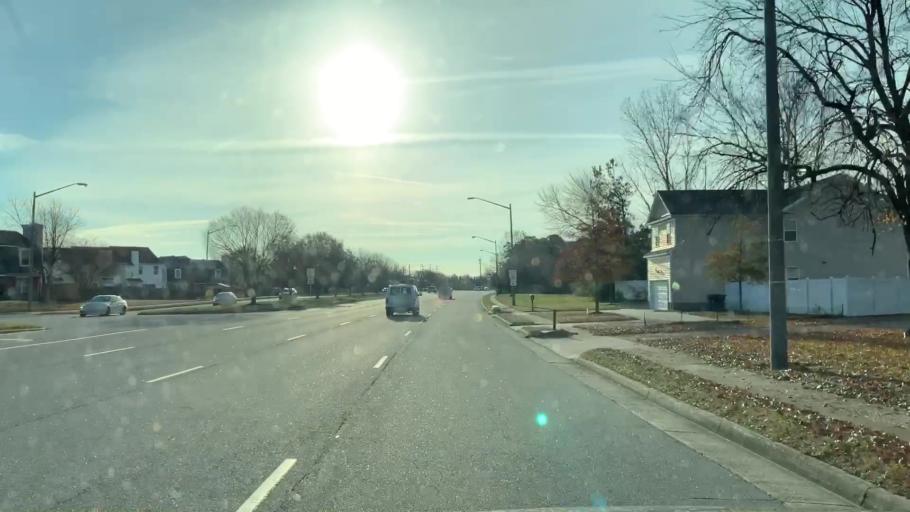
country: US
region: Virginia
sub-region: City of Chesapeake
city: Chesapeake
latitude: 36.7877
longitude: -76.1629
